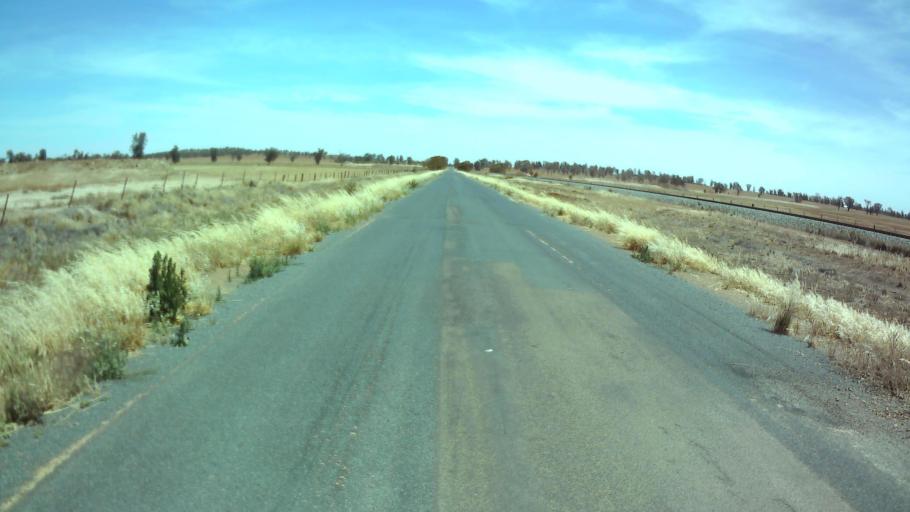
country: AU
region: New South Wales
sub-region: Weddin
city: Grenfell
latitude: -33.7588
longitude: 147.7618
